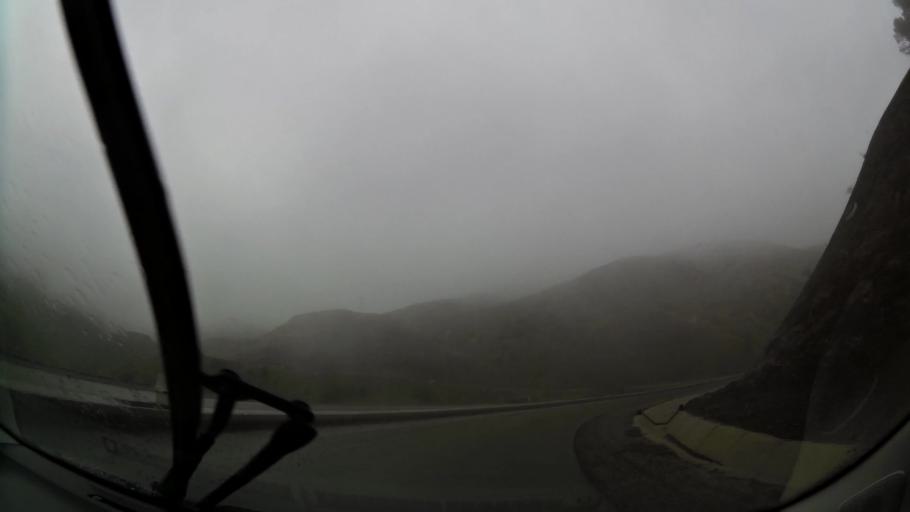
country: MA
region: Taza-Al Hoceima-Taounate
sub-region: Taza
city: Aknoul
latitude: 34.7758
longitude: -3.7890
